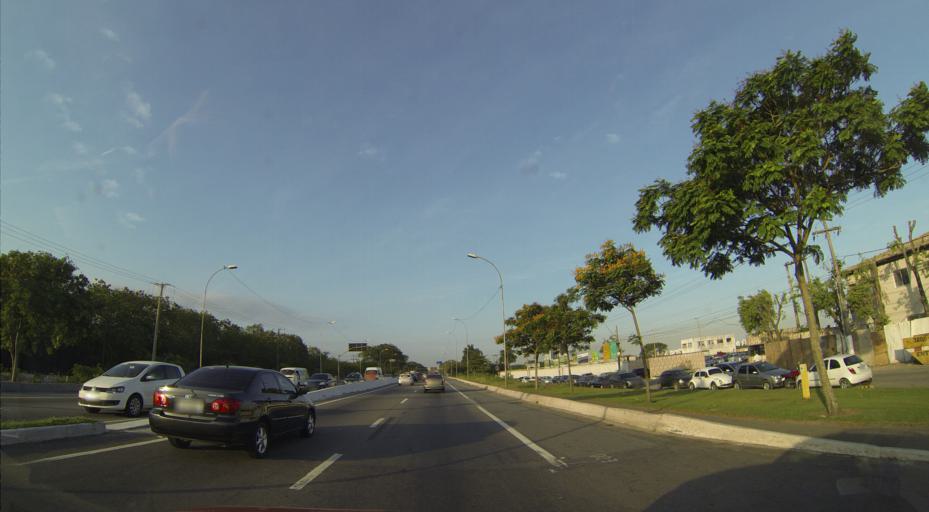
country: BR
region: Espirito Santo
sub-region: Vila Velha
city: Vila Velha
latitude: -20.2553
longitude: -40.2895
